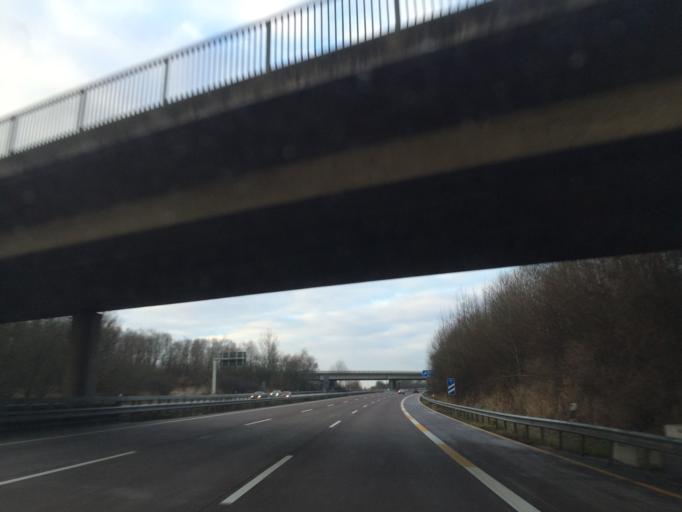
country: DE
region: Schleswig-Holstein
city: Siek
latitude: 53.6434
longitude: 10.2793
